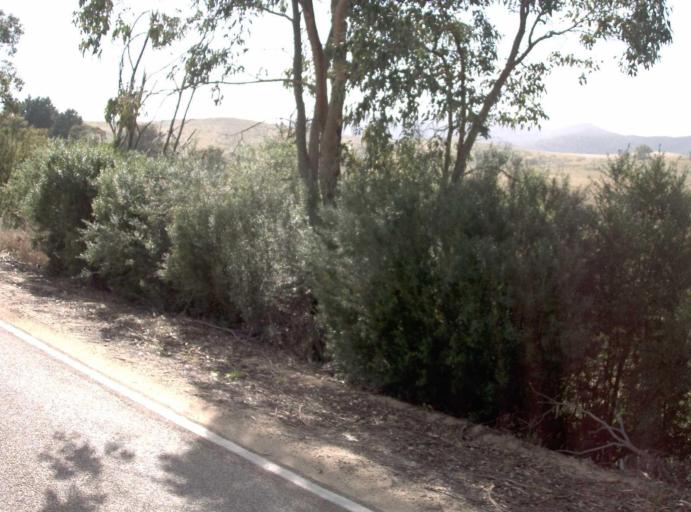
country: AU
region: Victoria
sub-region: East Gippsland
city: Lakes Entrance
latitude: -37.5160
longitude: 148.1648
